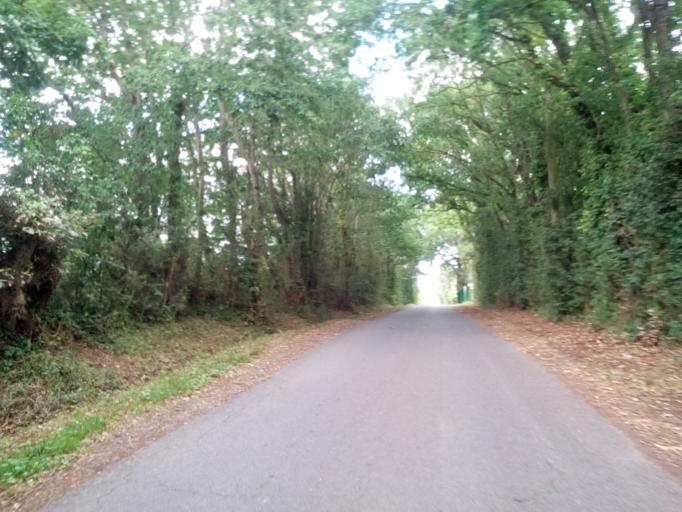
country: FR
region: Lower Normandy
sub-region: Departement du Calvados
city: Troarn
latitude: 49.1552
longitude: -0.1656
